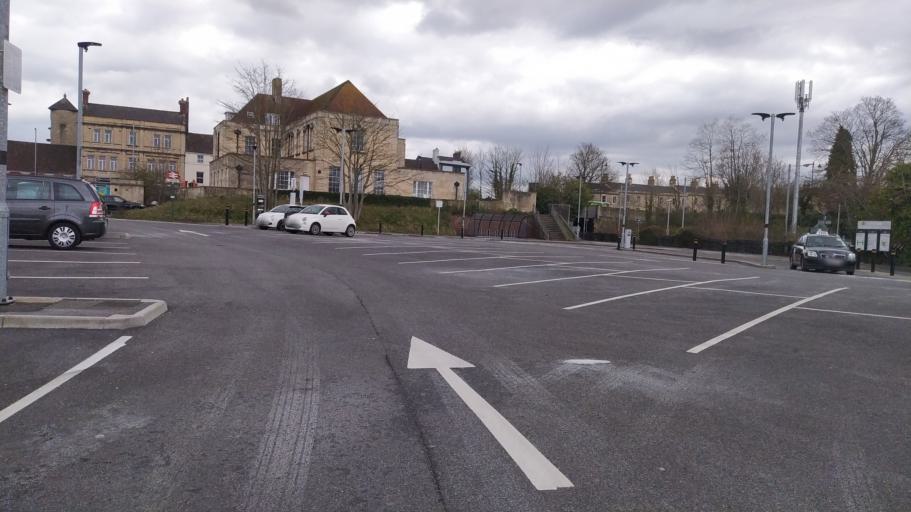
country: GB
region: England
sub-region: Wiltshire
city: Trowbridge
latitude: 51.3202
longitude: -2.2140
